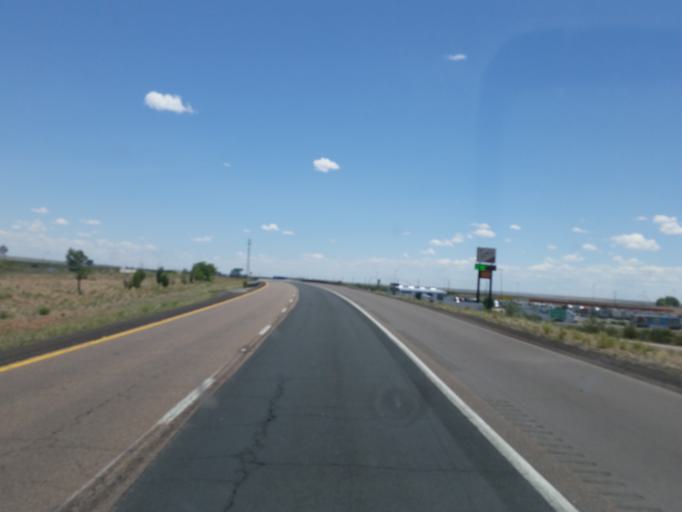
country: US
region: Arizona
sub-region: Navajo County
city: Winslow
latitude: 35.0187
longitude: -110.6764
